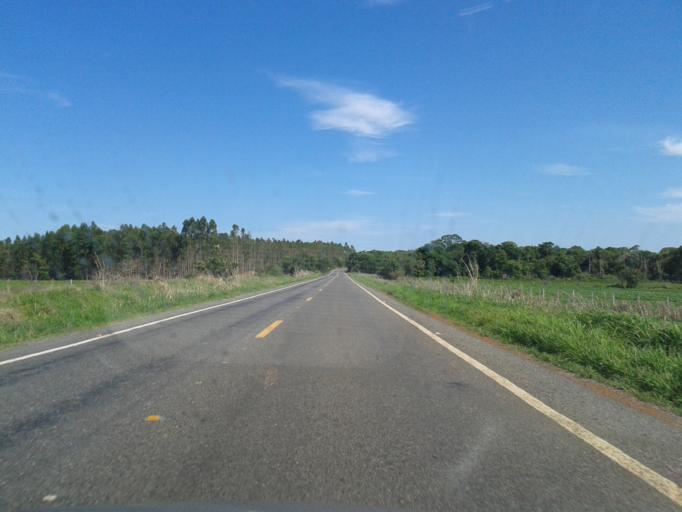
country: BR
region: Goias
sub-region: Piracanjuba
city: Piracanjuba
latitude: -17.3332
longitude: -48.7981
